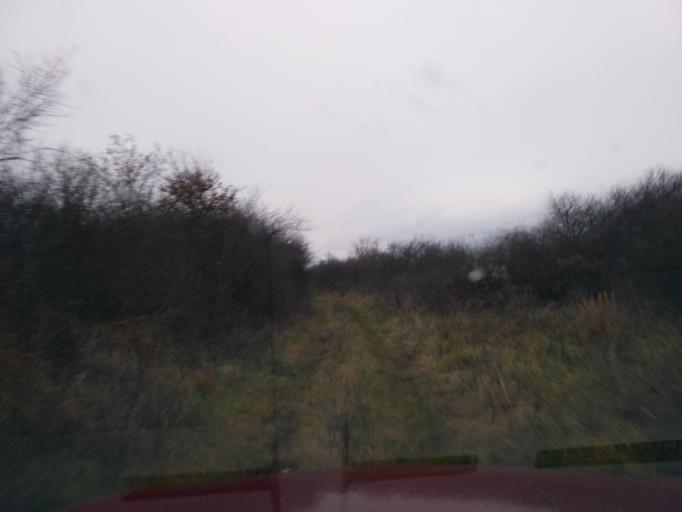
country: SK
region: Kosicky
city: Moldava nad Bodvou
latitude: 48.5593
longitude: 21.1419
